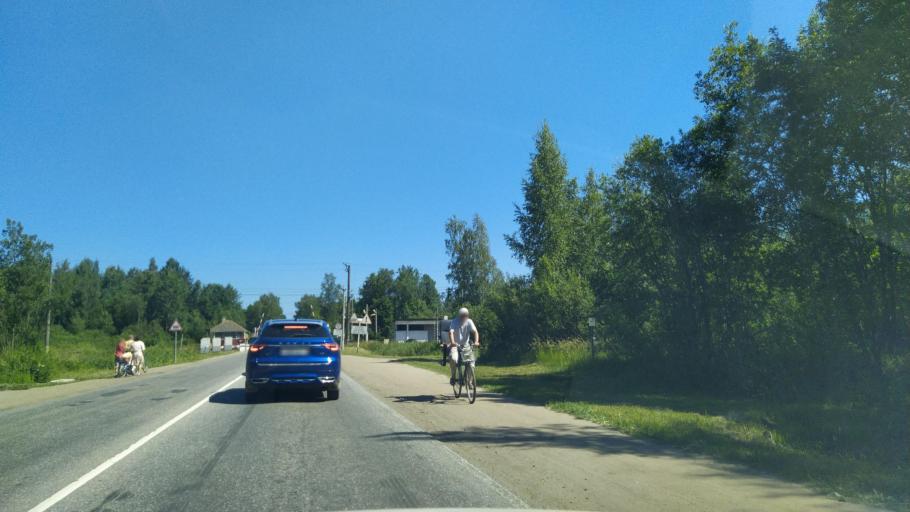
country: RU
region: Leningrad
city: Imeni Morozova
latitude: 59.9691
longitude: 31.0206
